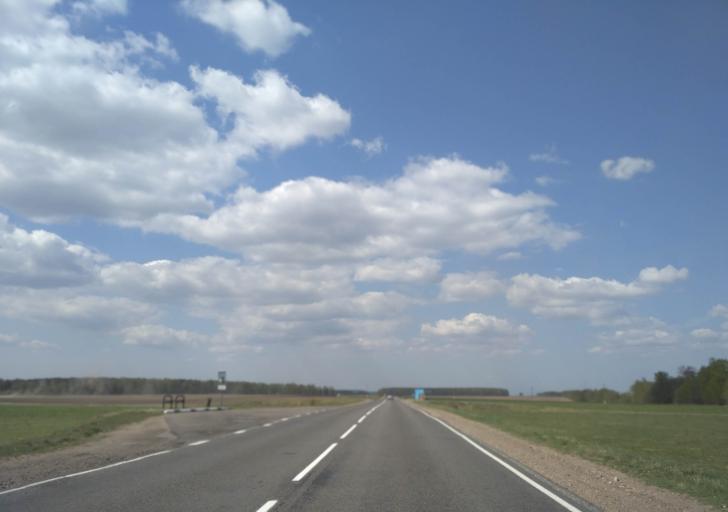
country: BY
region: Minsk
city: Vilyeyka
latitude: 54.5128
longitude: 27.0480
